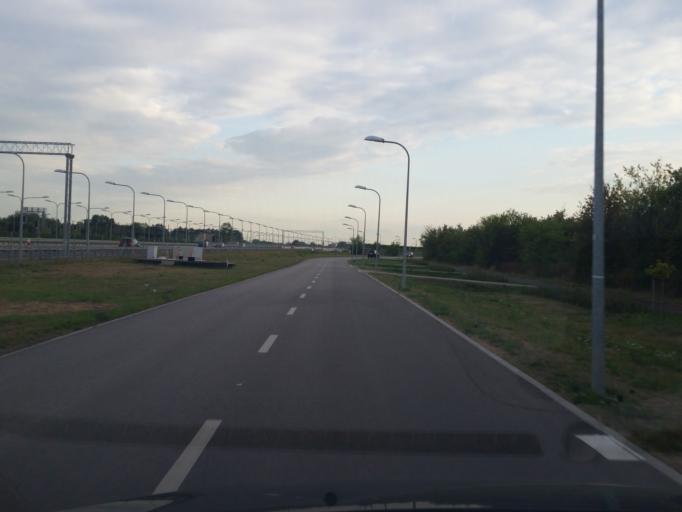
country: PL
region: Masovian Voivodeship
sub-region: Powiat piaseczynski
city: Mysiadlo
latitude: 52.1441
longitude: 20.9881
